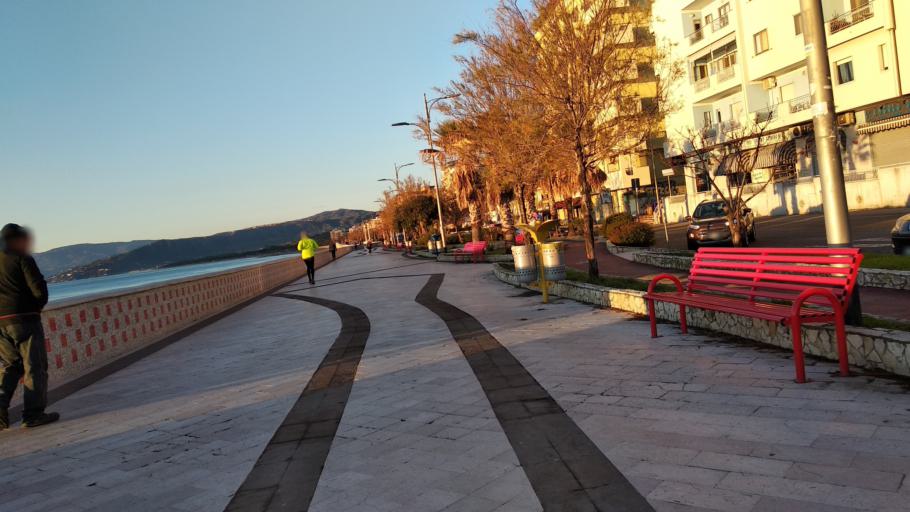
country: IT
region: Calabria
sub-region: Provincia di Catanzaro
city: Roccelletta
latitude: 38.8245
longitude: 16.6224
